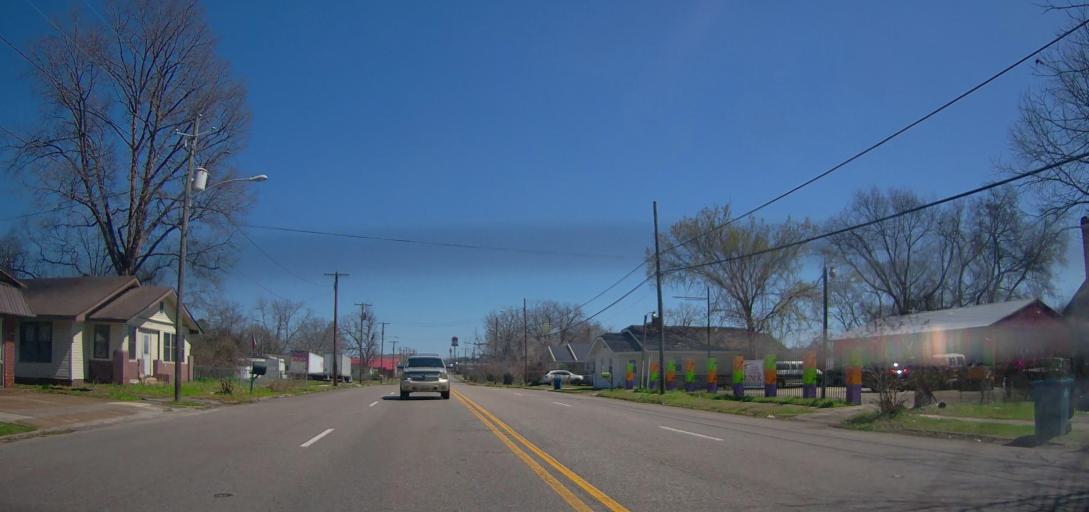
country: US
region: Alabama
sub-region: Etowah County
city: Attalla
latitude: 34.0178
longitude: -86.0829
